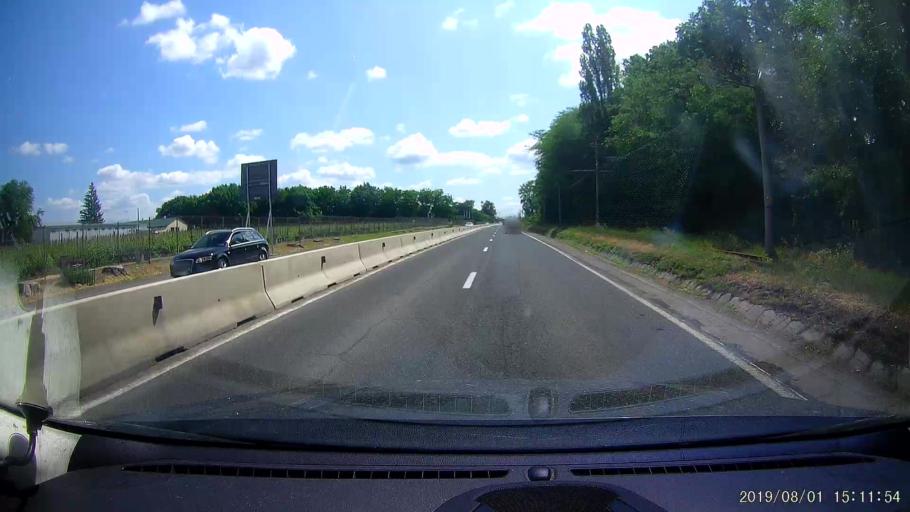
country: RO
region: Braila
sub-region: Comuna Chiscani
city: Chiscani
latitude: 45.2125
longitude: 27.9194
